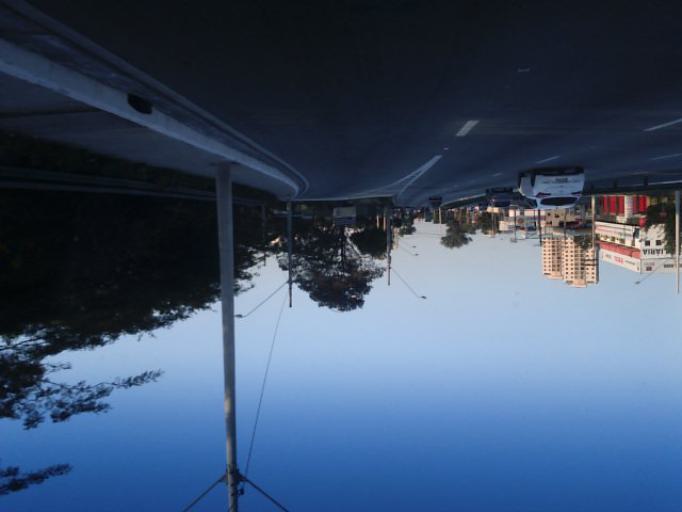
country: BR
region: Sao Paulo
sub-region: Sao Jose Dos Campos
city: Sao Jose dos Campos
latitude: -23.2221
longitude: -45.9011
